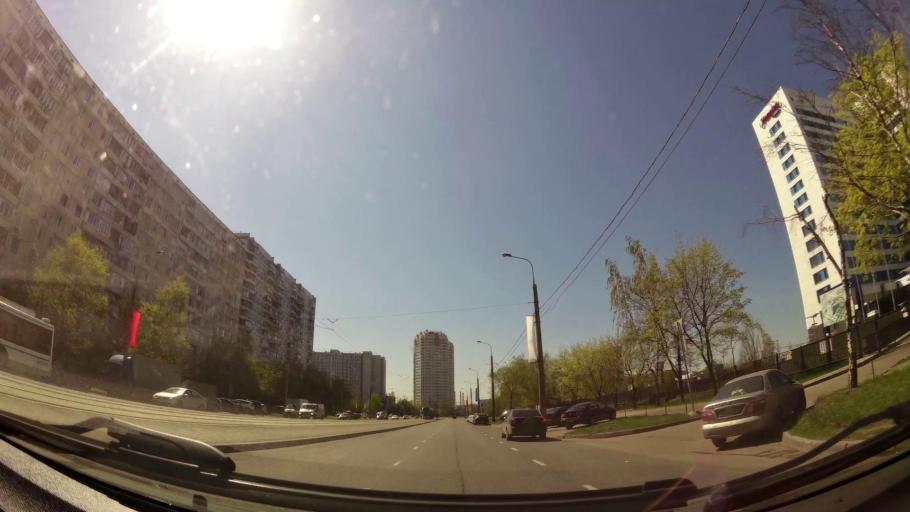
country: RU
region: Moscow
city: Strogino
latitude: 55.8027
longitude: 37.3919
